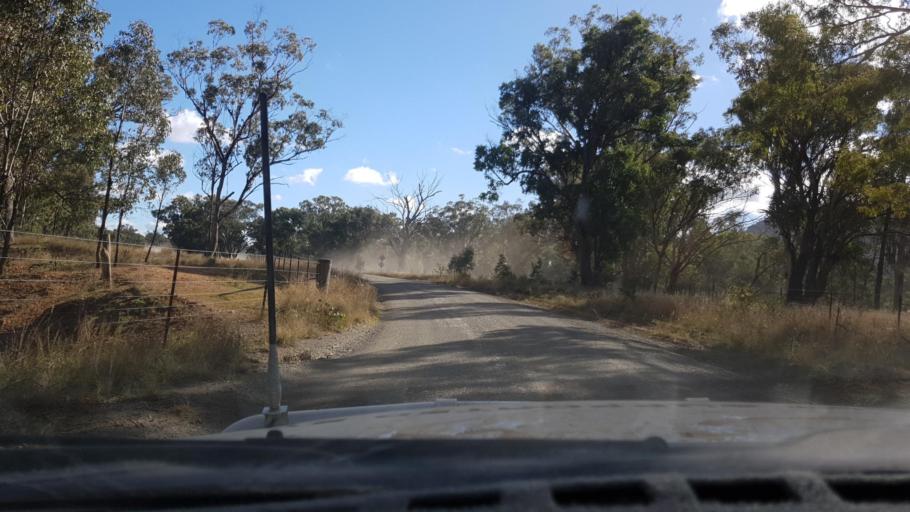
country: AU
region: New South Wales
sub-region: Tamworth Municipality
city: Manilla
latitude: -30.5993
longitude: 150.4976
